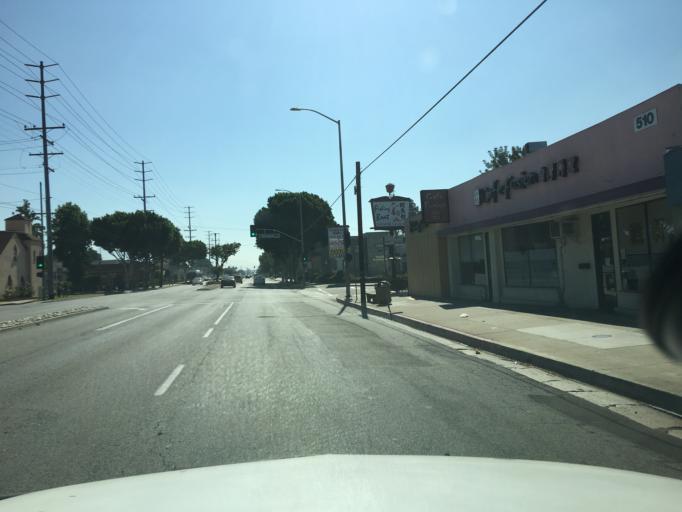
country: US
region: California
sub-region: Los Angeles County
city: North El Monte
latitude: 34.1090
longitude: -118.0190
